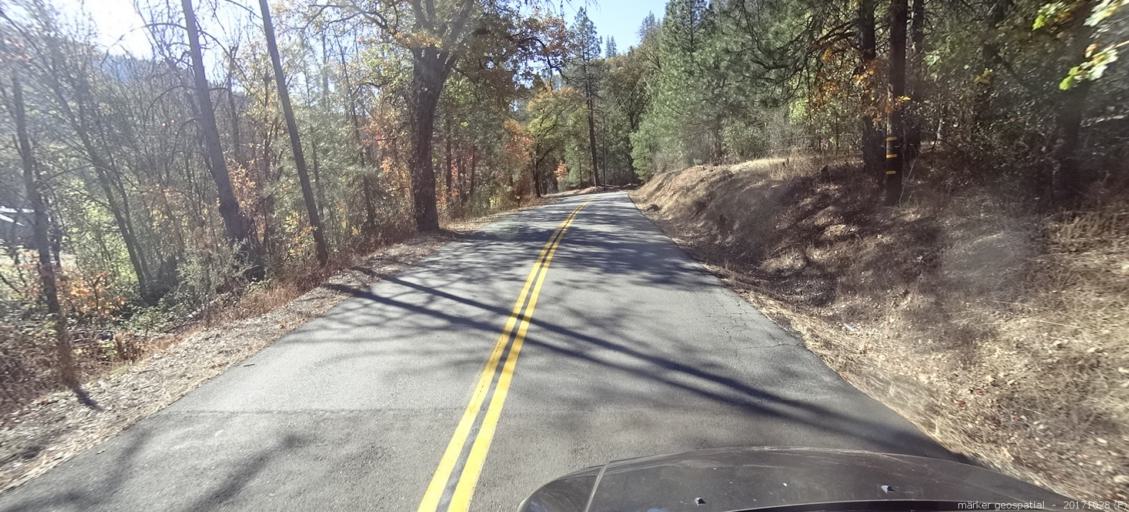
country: US
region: California
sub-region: Trinity County
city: Lewiston
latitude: 40.7569
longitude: -122.6166
